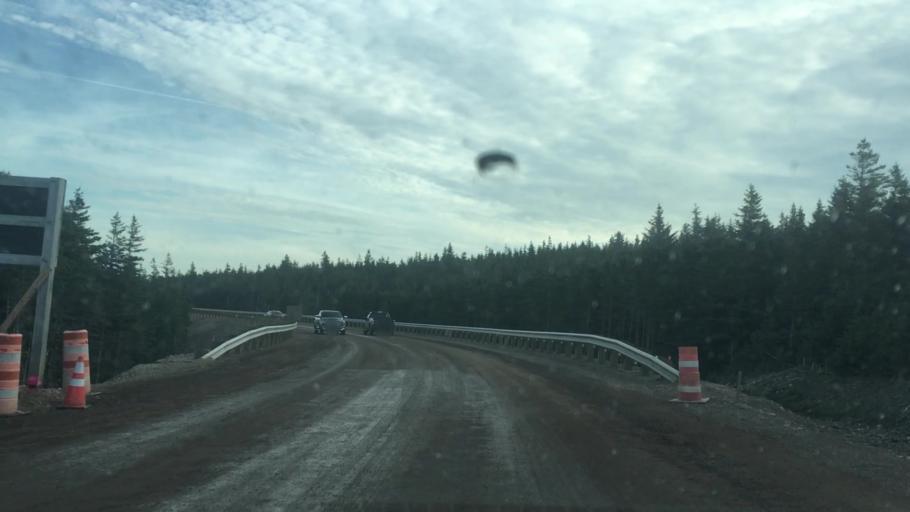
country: CA
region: Nova Scotia
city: Sydney Mines
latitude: 46.8066
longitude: -60.8442
